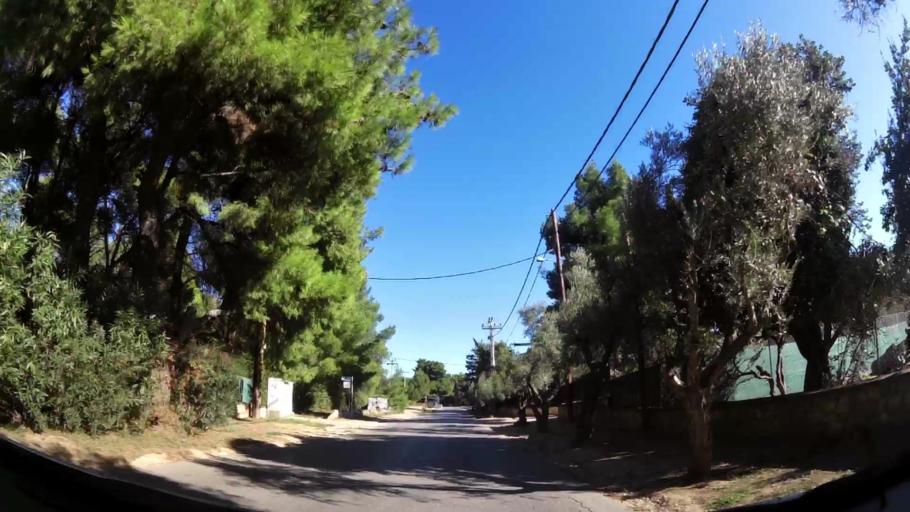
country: GR
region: Attica
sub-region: Nomarchia Anatolikis Attikis
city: Varybobi
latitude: 38.1231
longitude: 23.7927
